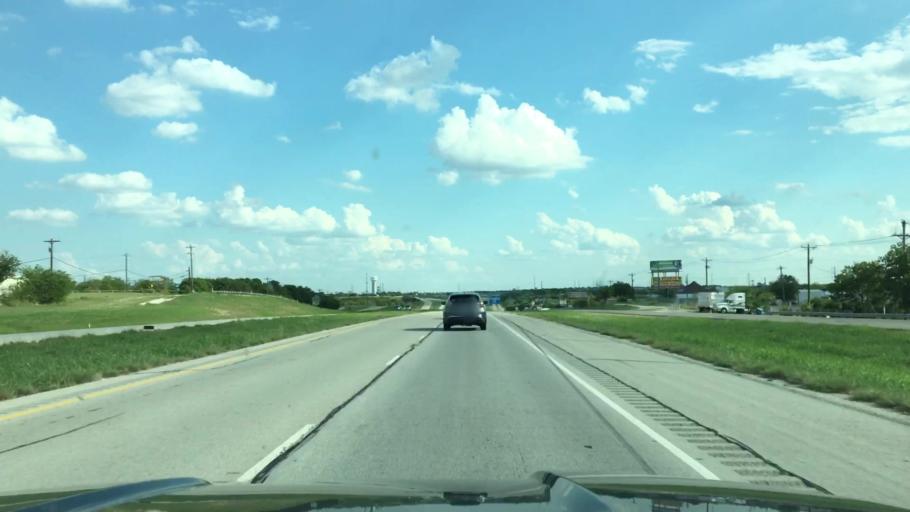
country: US
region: Texas
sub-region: Tarrant County
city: Pecan Acres
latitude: 32.9859
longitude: -97.4282
